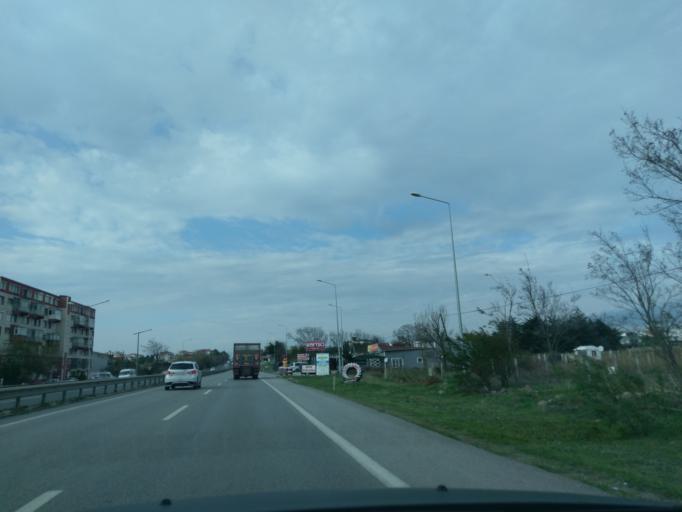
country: TR
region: Istanbul
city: Celaliye
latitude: 41.0476
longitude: 28.4008
